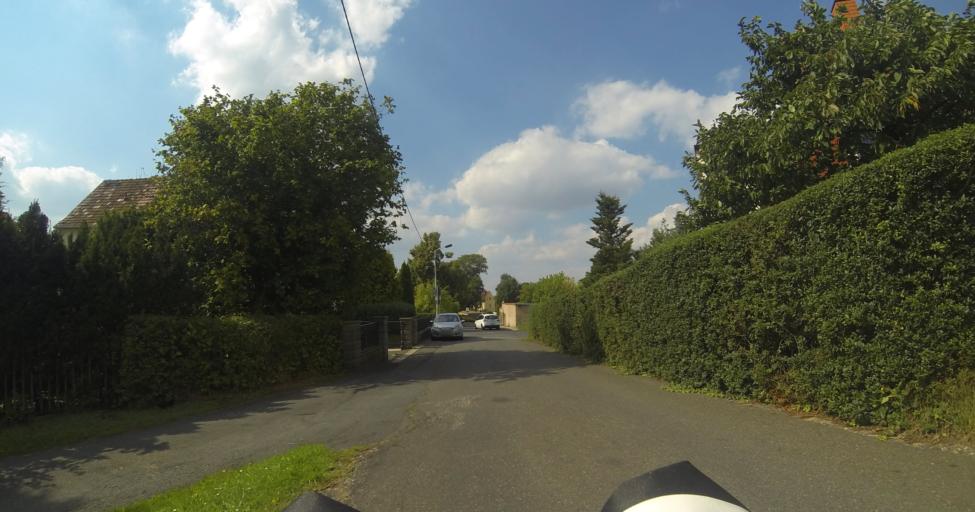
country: DE
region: Saxony
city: Grossenhain
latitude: 51.2852
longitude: 13.5323
